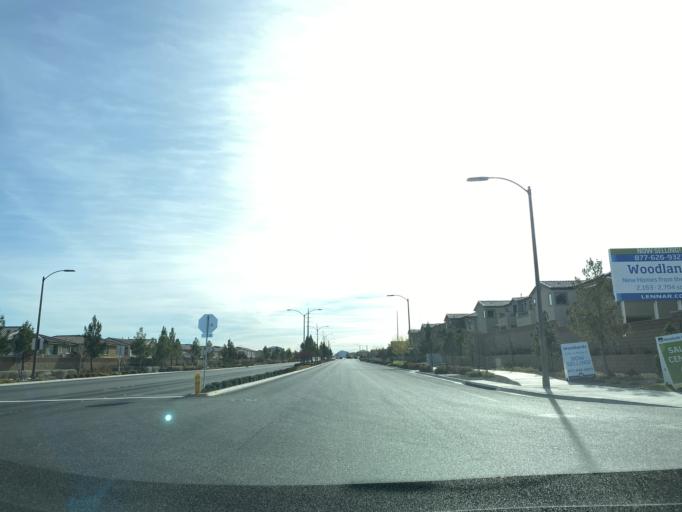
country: US
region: Nevada
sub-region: Clark County
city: Summerlin South
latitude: 36.3105
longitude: -115.3150
